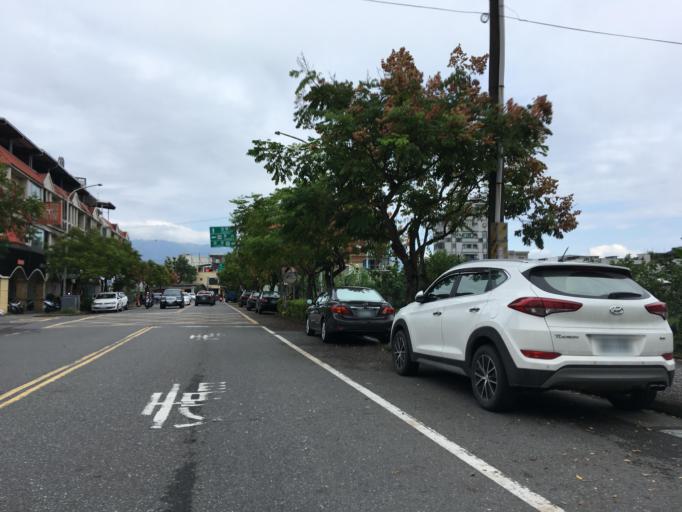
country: TW
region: Taiwan
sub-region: Yilan
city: Yilan
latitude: 24.7413
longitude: 121.7535
